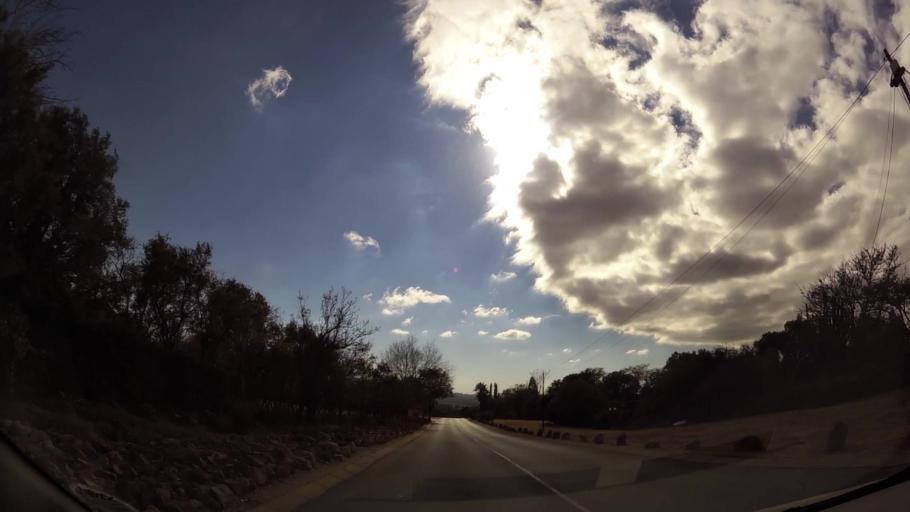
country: ZA
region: Gauteng
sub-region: West Rand District Municipality
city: Muldersdriseloop
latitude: -26.0822
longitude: 27.8555
